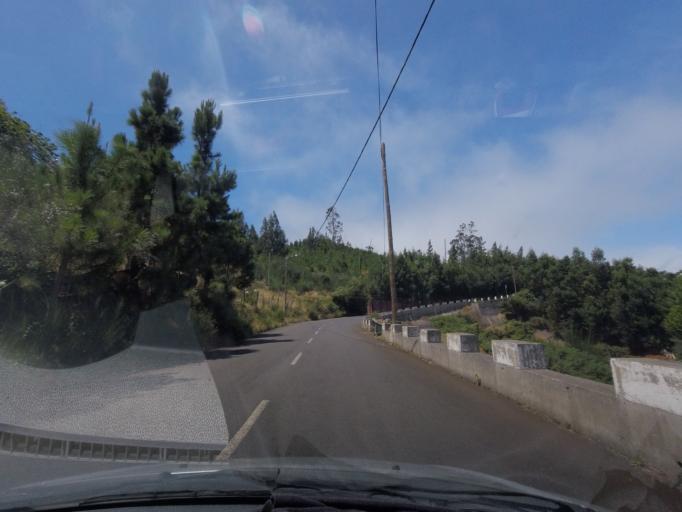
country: PT
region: Madeira
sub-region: Santa Cruz
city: Camacha
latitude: 32.6855
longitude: -16.8273
